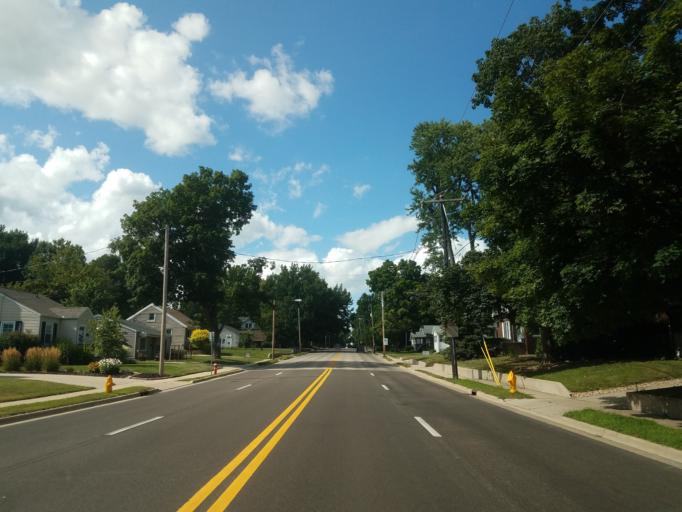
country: US
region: Illinois
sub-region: McLean County
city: Bloomington
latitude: 40.4952
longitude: -88.9820
